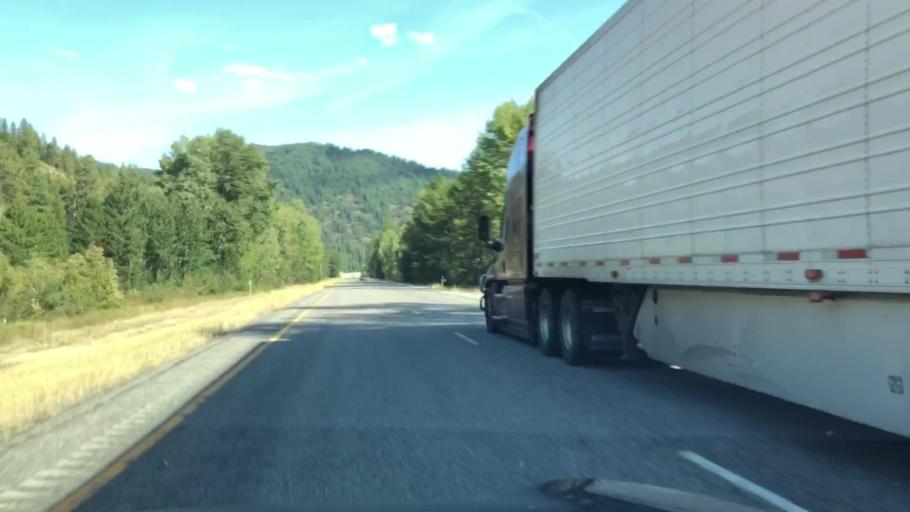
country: US
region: Montana
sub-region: Sanders County
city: Thompson Falls
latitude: 47.3588
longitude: -115.3113
